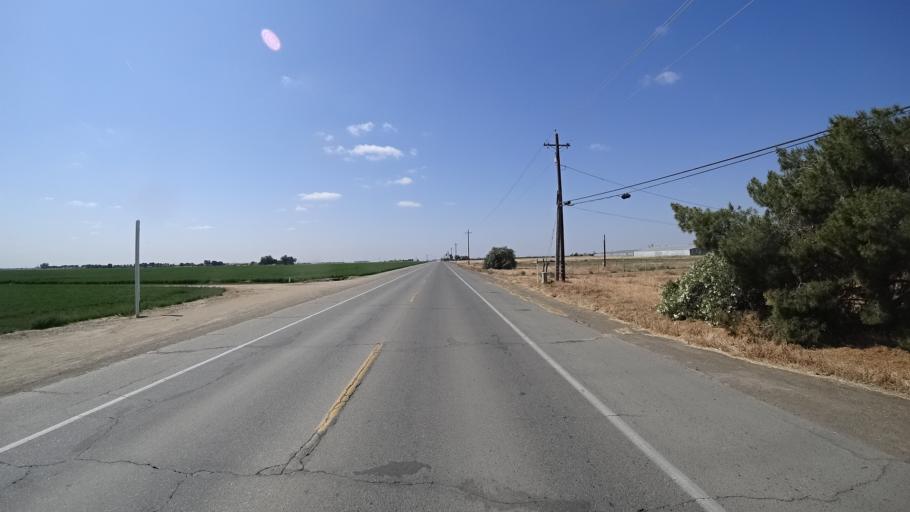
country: US
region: California
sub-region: Kings County
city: Home Garden
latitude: 36.2773
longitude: -119.6370
